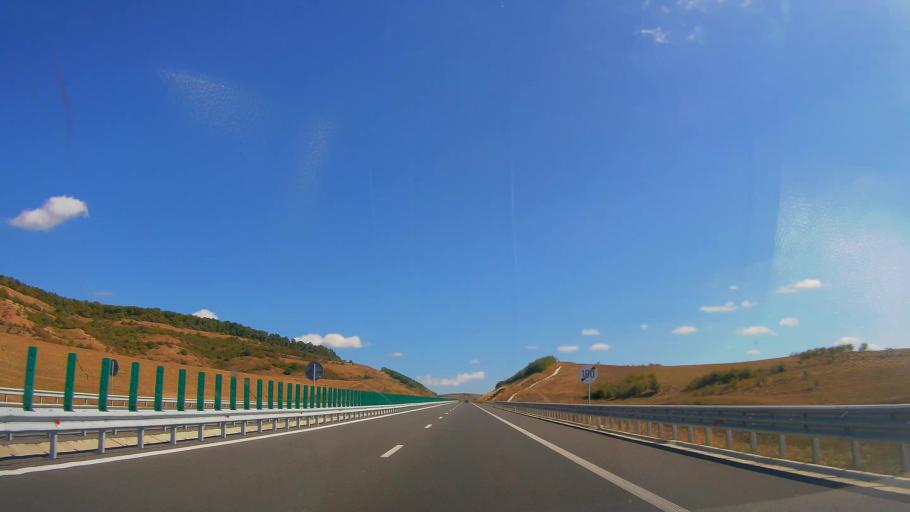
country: RO
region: Cluj
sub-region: Comuna Floresti
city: Luna de Sus
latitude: 46.7767
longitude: 23.3938
